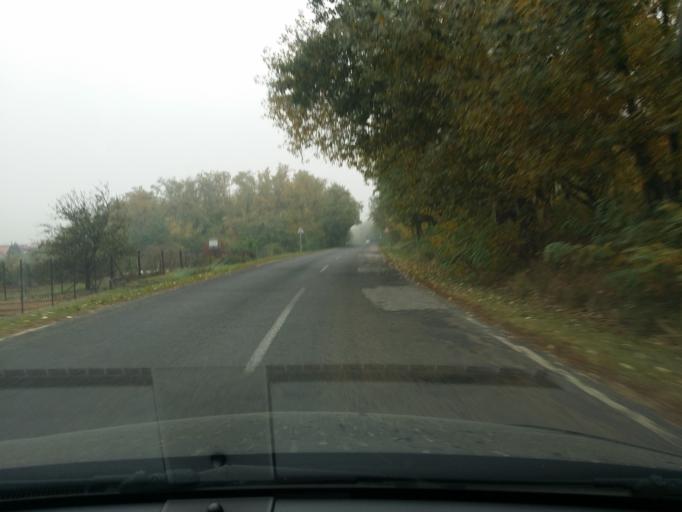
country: HU
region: Szabolcs-Szatmar-Bereg
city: Nyirbogdany
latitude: 48.0766
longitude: 21.8597
